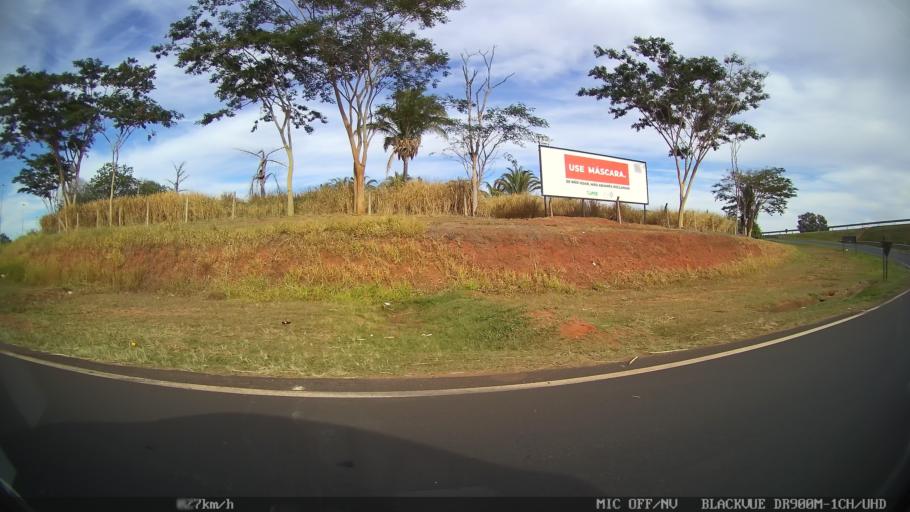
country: BR
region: Sao Paulo
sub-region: Catanduva
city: Catanduva
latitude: -21.1101
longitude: -48.9619
